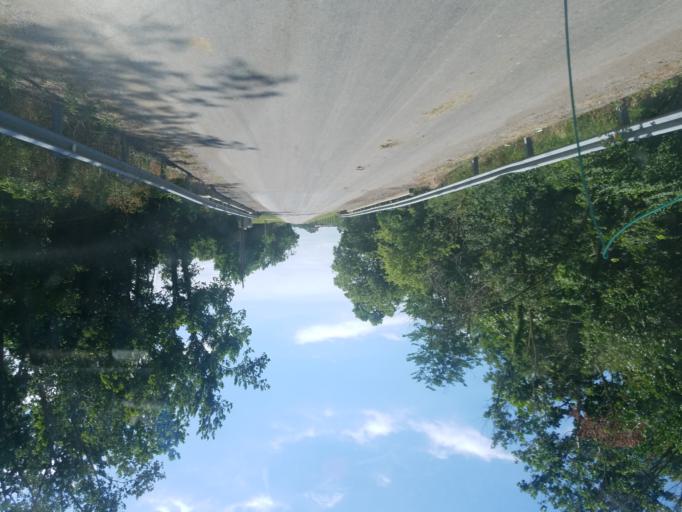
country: US
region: Indiana
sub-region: Allen County
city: Harlan
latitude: 41.1837
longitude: -84.8697
